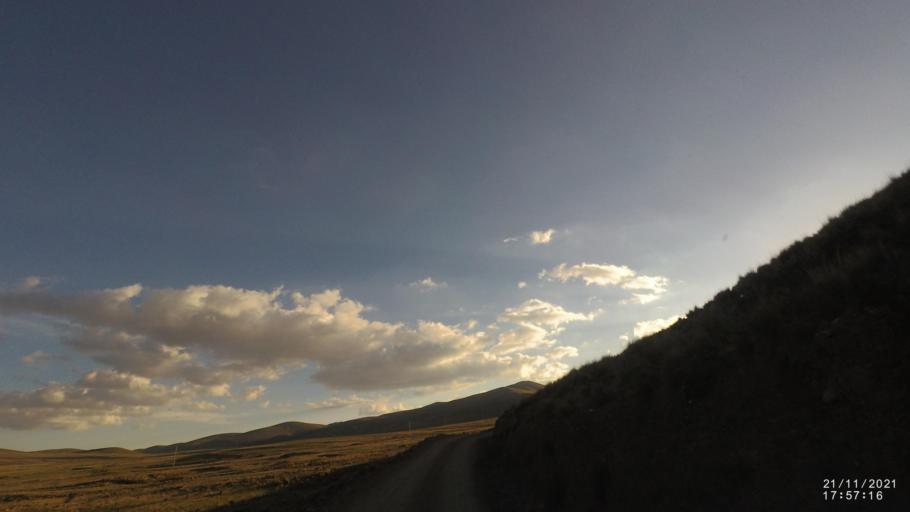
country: BO
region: Cochabamba
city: Cochabamba
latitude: -17.2271
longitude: -66.2321
